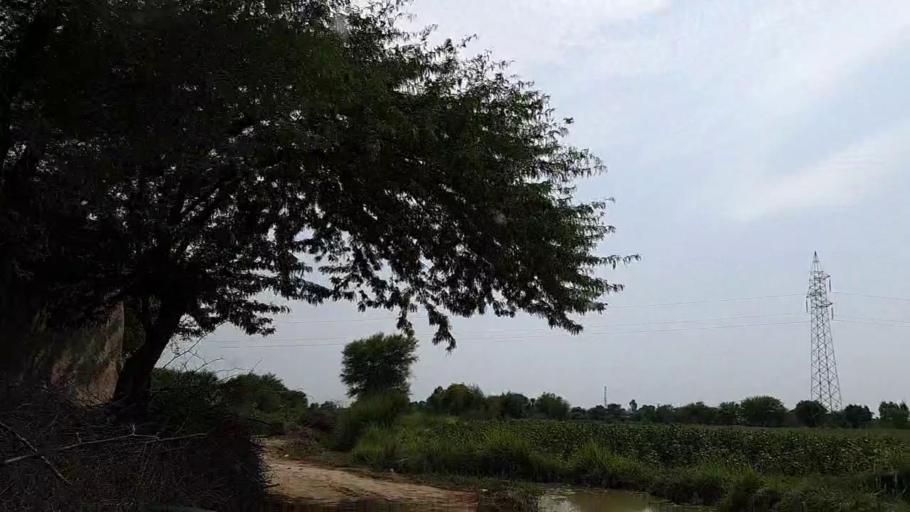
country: PK
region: Sindh
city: Khanpur
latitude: 27.8540
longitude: 69.4240
